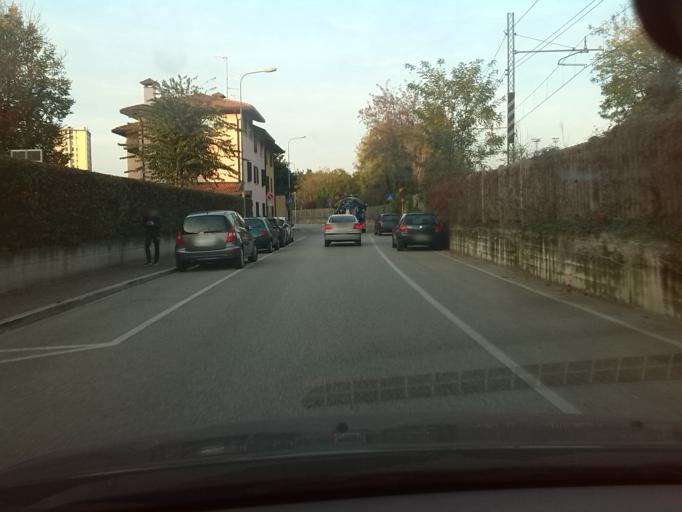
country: IT
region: Friuli Venezia Giulia
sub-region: Provincia di Udine
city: Udine
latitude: 46.0510
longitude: 13.2300
